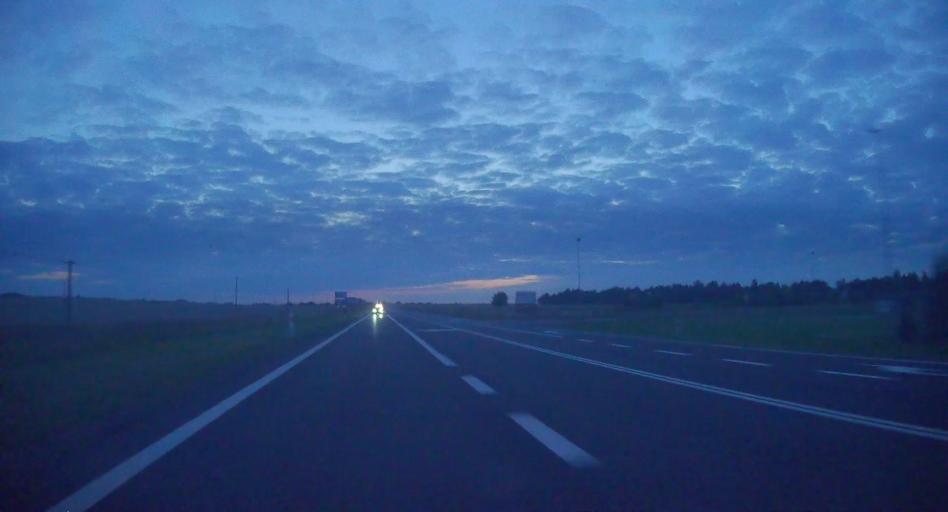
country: PL
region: Silesian Voivodeship
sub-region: Powiat klobucki
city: Klobuck
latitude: 50.8867
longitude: 18.9771
